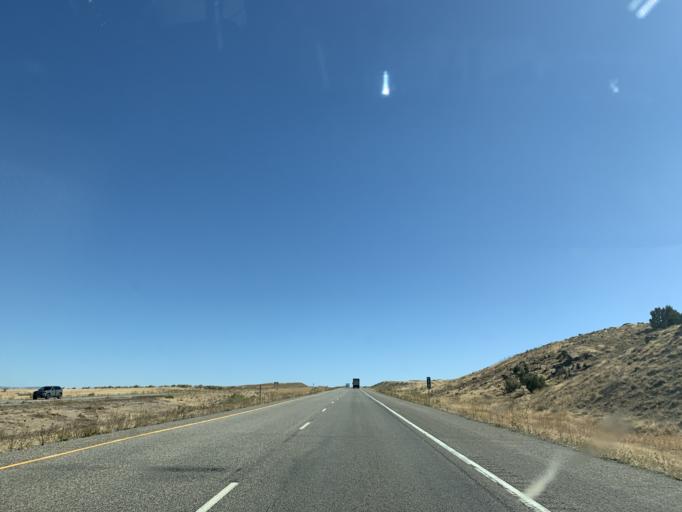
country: US
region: Colorado
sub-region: Mesa County
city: Loma
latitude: 39.2210
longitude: -108.8858
